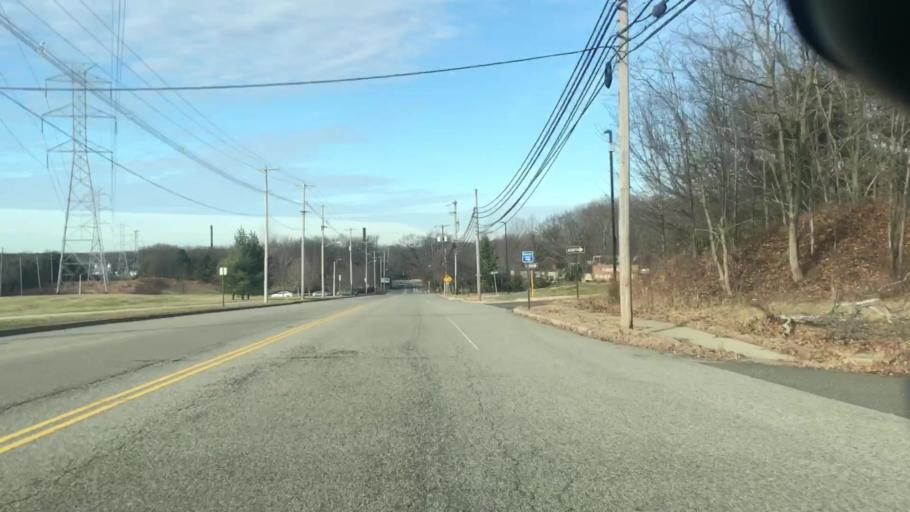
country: US
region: New Jersey
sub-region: Middlesex County
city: South Amboy
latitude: 40.4777
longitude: -74.3074
